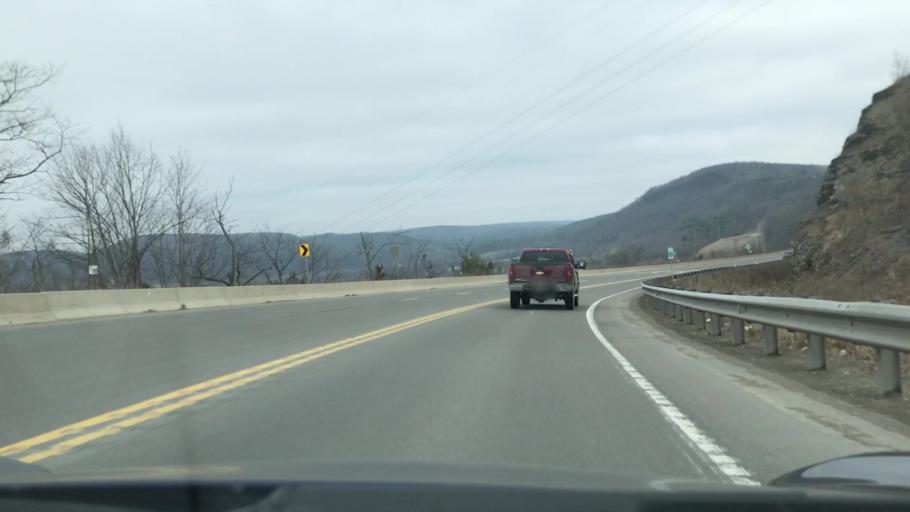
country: US
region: Pennsylvania
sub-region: Bradford County
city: Towanda
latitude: 41.7616
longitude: -76.3695
